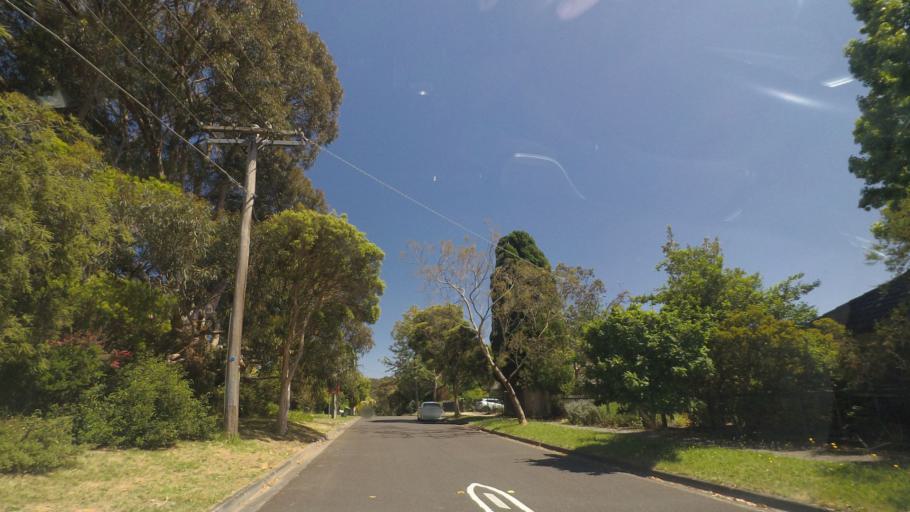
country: AU
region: Victoria
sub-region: Yarra Ranges
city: Montrose
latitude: -37.8086
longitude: 145.3539
